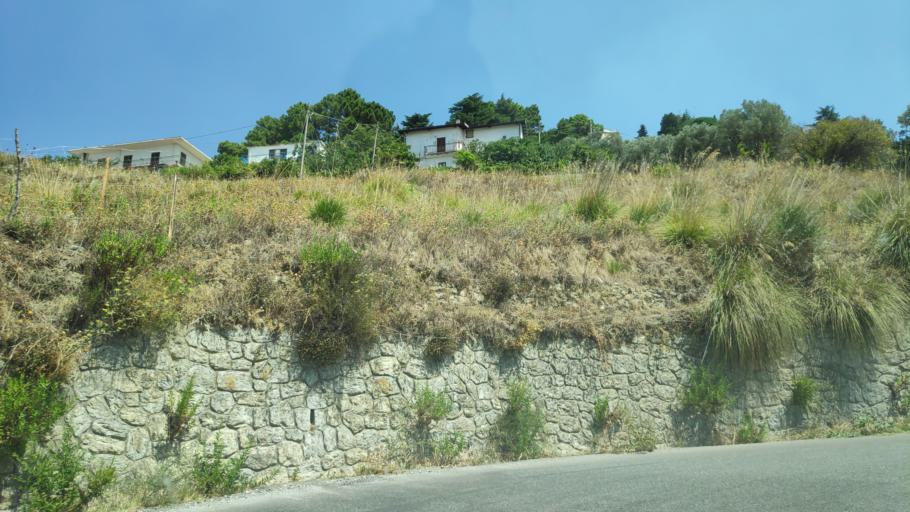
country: IT
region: Calabria
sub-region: Provincia di Reggio Calabria
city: Bova
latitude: 37.9931
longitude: 15.9288
